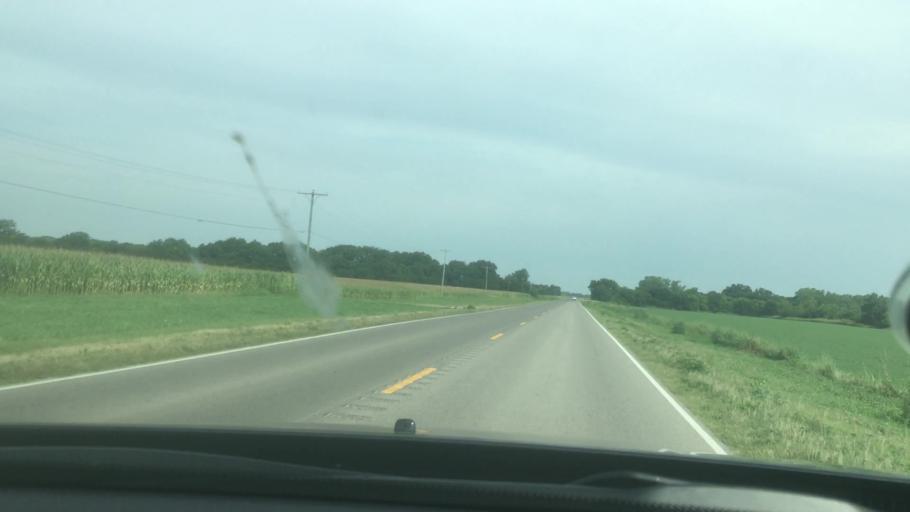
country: US
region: Oklahoma
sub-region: Garvin County
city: Maysville
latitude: 34.7824
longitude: -97.3302
